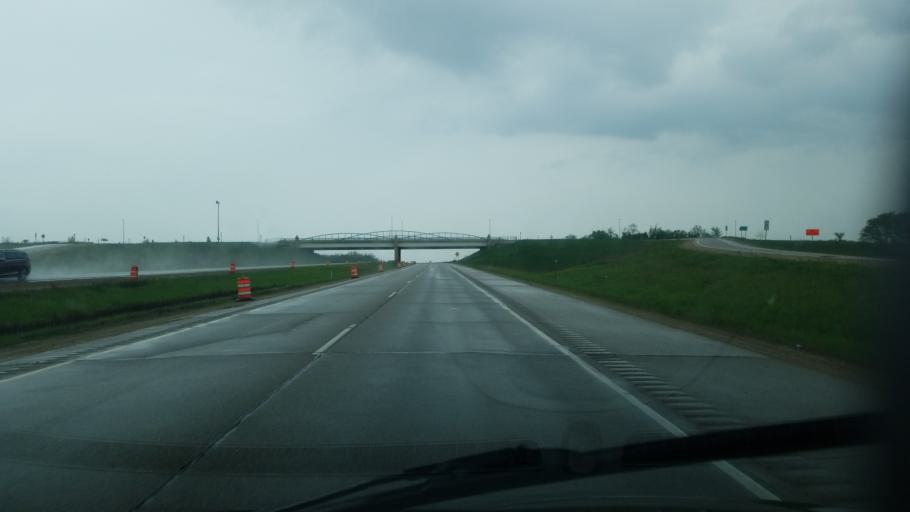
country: US
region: Wisconsin
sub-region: Dane County
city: Madison
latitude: 43.0071
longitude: -89.3832
